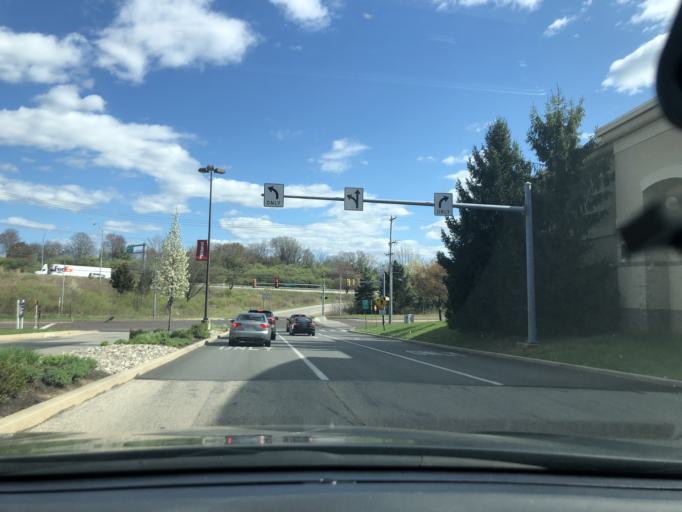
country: US
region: Pennsylvania
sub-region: Montgomery County
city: Plymouth Meeting
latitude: 40.1030
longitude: -75.2921
